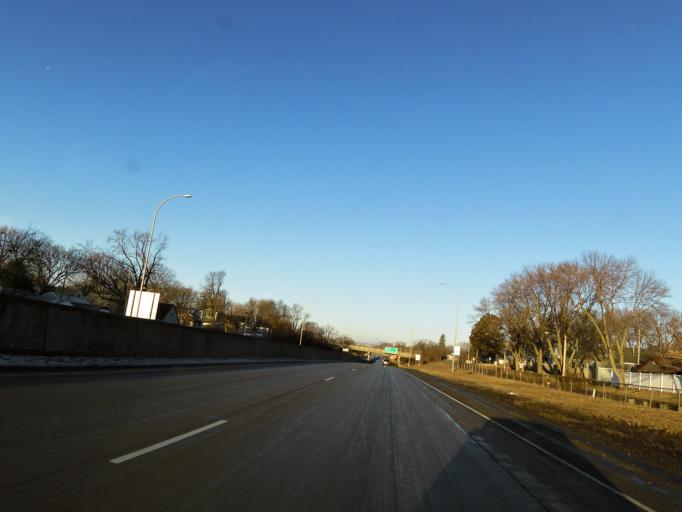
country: US
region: Minnesota
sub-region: Dakota County
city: Mendota Heights
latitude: 44.8985
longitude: -93.2085
